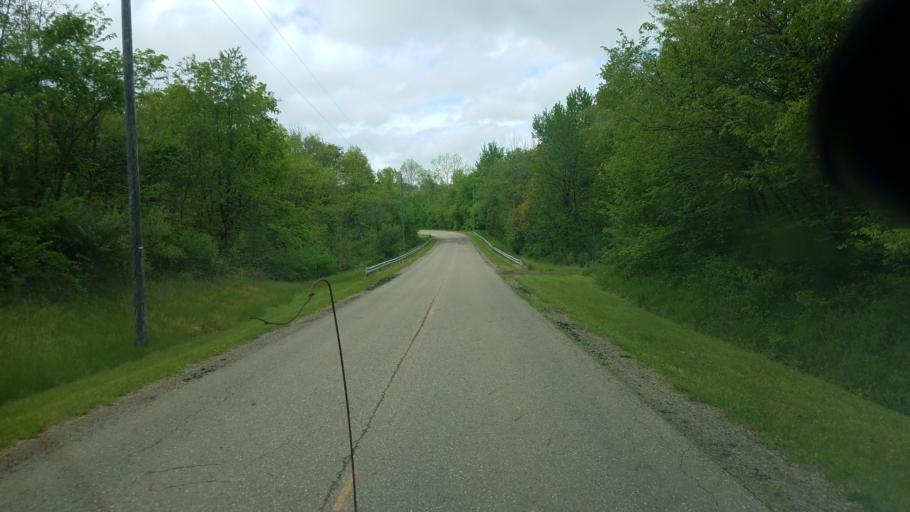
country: US
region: Ohio
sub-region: Tuscarawas County
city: Dover
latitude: 40.5931
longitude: -81.4106
